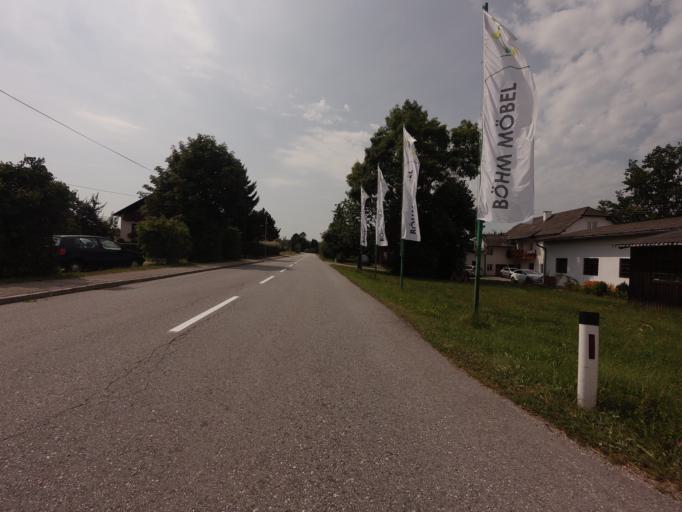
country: AT
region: Upper Austria
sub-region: Politischer Bezirk Urfahr-Umgebung
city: Reichenthal
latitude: 48.5523
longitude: 14.4502
